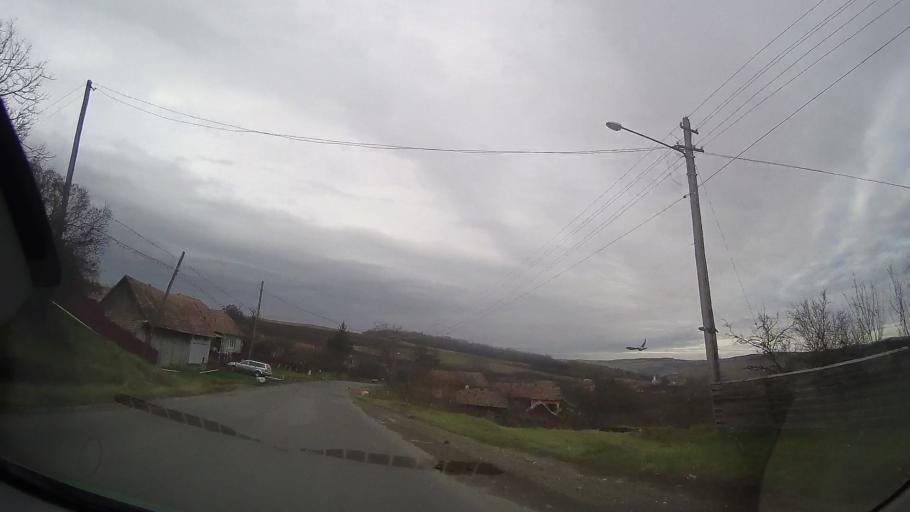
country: RO
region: Bistrita-Nasaud
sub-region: Comuna Silvasu de Campie
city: Silvasu de Campie
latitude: 46.7782
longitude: 24.3101
